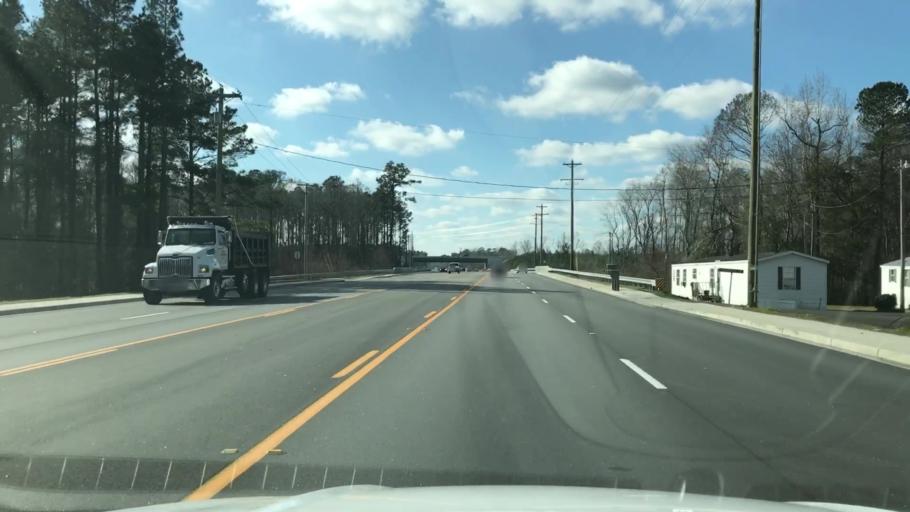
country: US
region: South Carolina
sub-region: Horry County
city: Socastee
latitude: 33.6570
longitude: -79.0160
